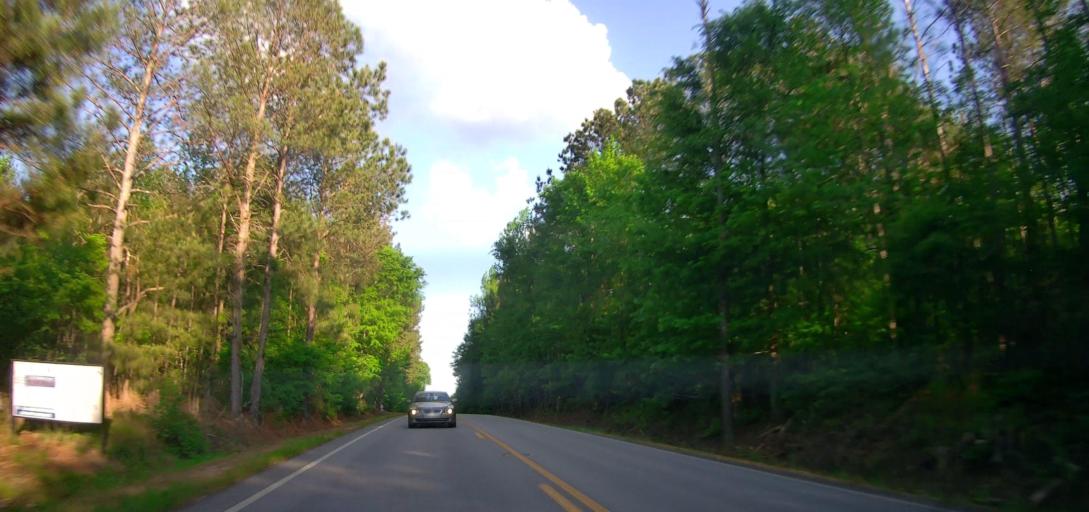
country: US
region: Georgia
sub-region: Jasper County
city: Monticello
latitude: 33.3913
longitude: -83.5715
